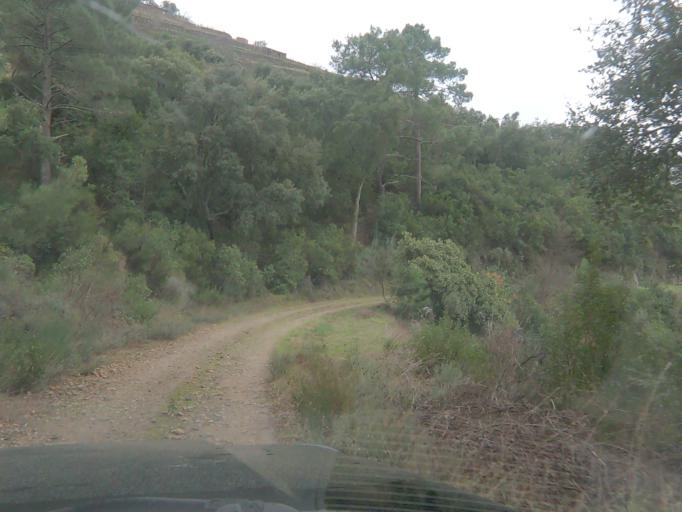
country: PT
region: Vila Real
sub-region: Vila Real
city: Vila Real
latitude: 41.2463
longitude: -7.7464
